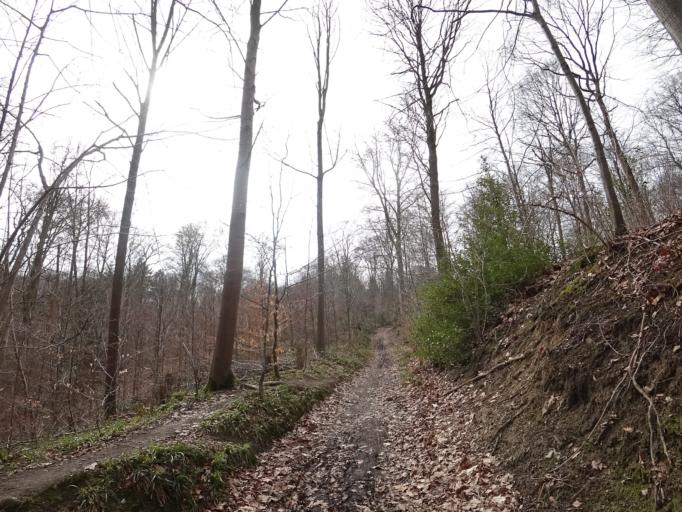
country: BE
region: Wallonia
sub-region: Province de Namur
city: Namur
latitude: 50.4431
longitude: 4.8288
